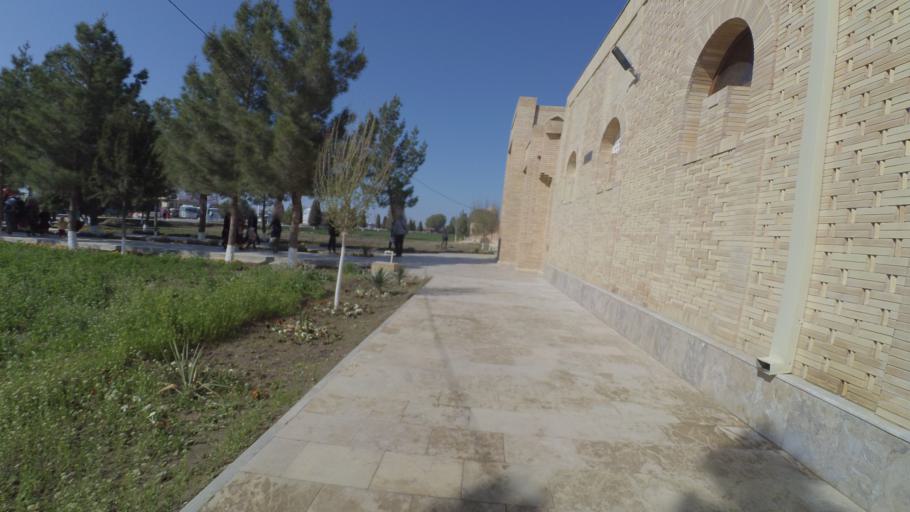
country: UZ
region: Bukhara
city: Kogon
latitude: 39.8006
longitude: 64.5390
